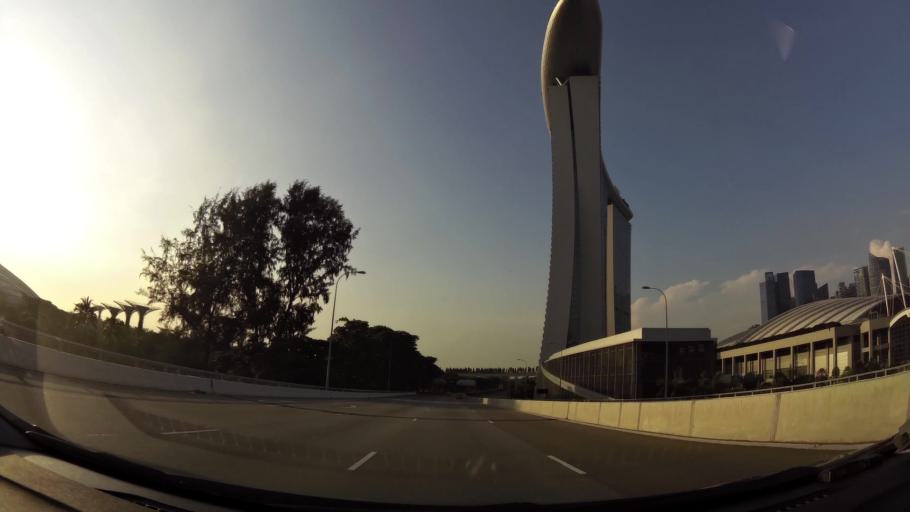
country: SG
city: Singapore
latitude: 1.2864
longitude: 103.8616
